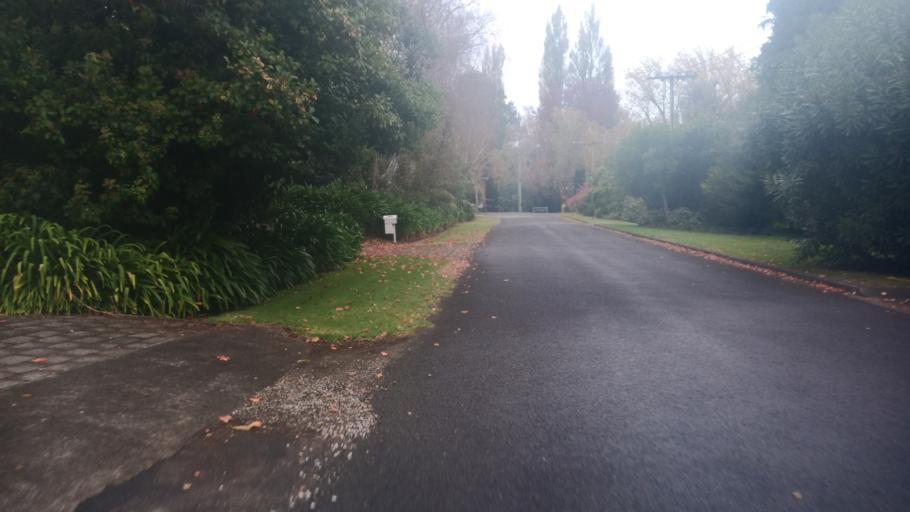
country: NZ
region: Gisborne
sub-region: Gisborne District
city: Gisborne
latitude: -38.6650
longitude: 178.0400
